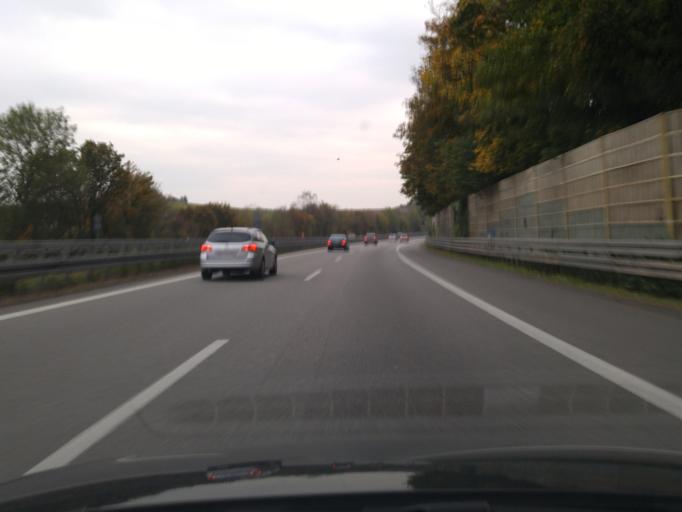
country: DE
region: Baden-Wuerttemberg
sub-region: Regierungsbezirk Stuttgart
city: Bretzfeld
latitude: 49.1714
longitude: 9.3798
